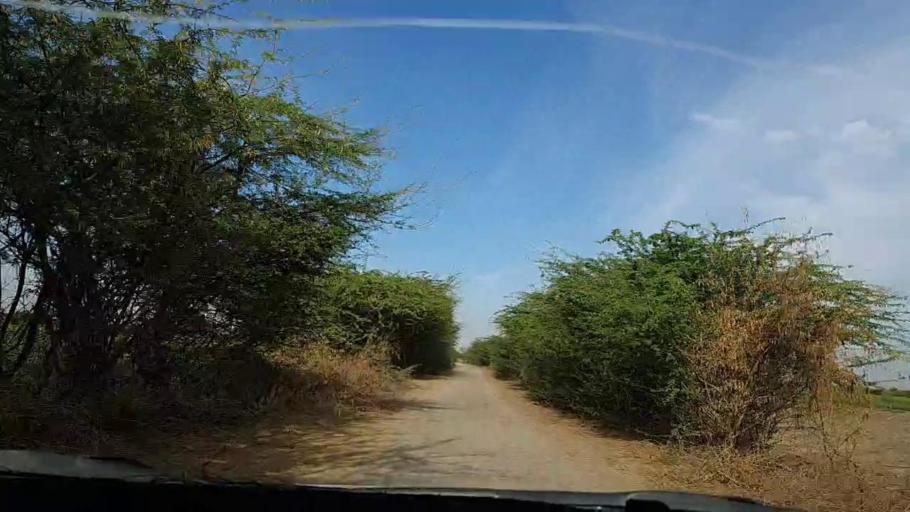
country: PK
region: Sindh
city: Dhoro Naro
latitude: 25.4775
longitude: 69.5393
